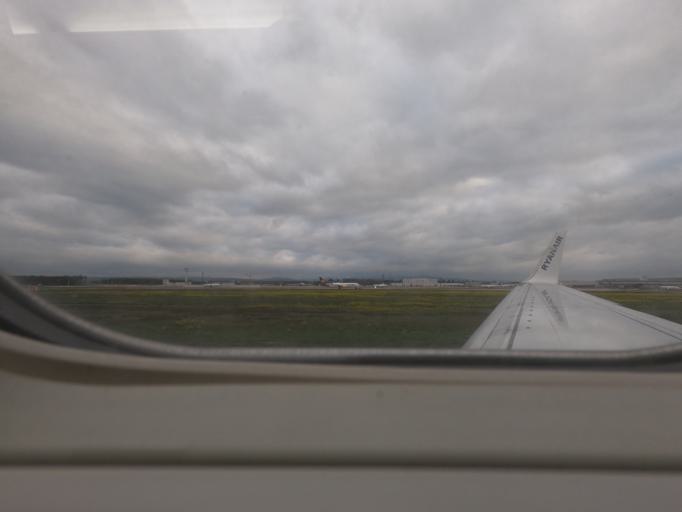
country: DE
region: Hesse
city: Kelsterbach
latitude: 50.0298
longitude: 8.5334
